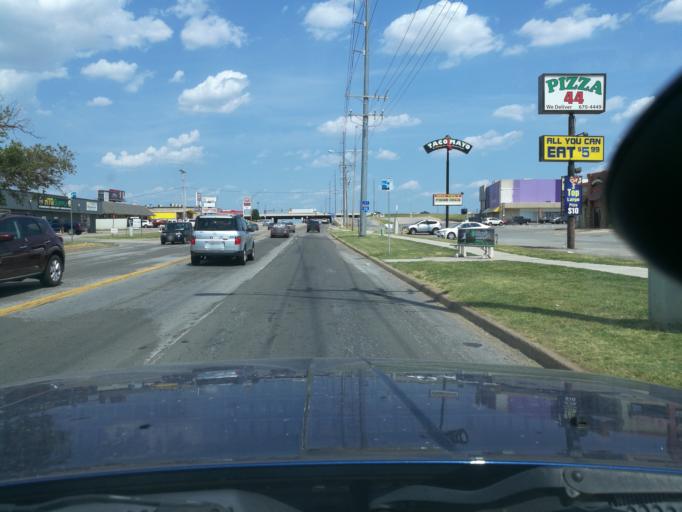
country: US
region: Oklahoma
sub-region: Oklahoma County
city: Oklahoma City
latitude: 35.4208
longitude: -97.4918
